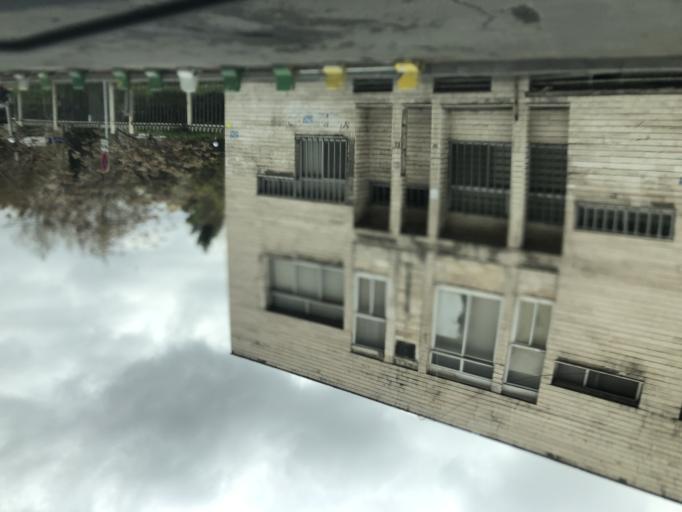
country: IR
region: Tehran
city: Tajrish
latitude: 35.7783
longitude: 51.4649
